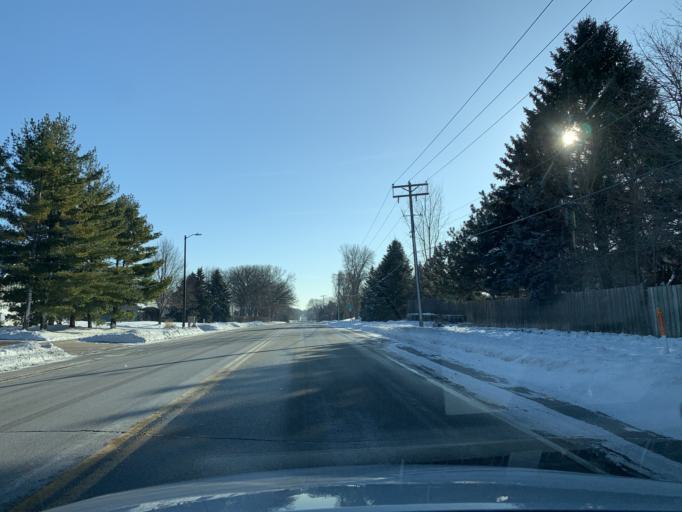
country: US
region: Minnesota
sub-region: Scott County
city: Savage
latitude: 44.8307
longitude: -93.3585
